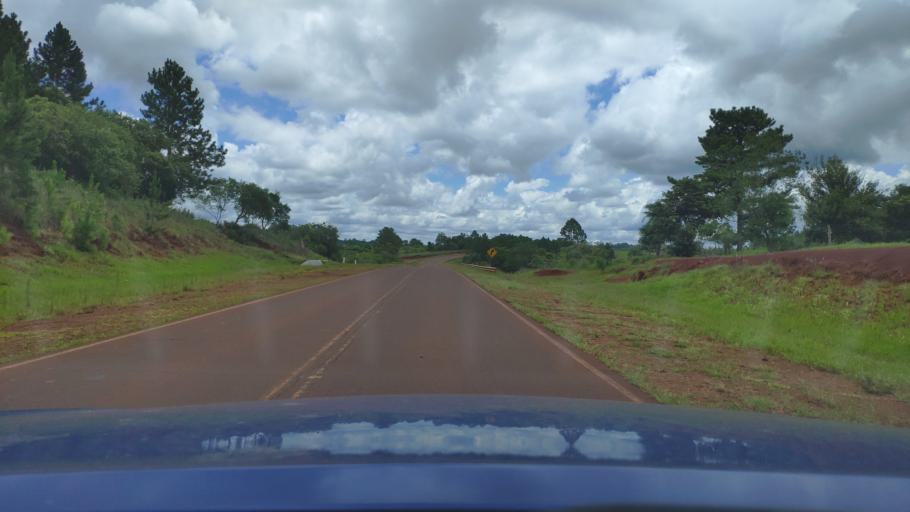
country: AR
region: Misiones
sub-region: Departamento de San Javier
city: San Javier
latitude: -27.8465
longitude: -55.2432
